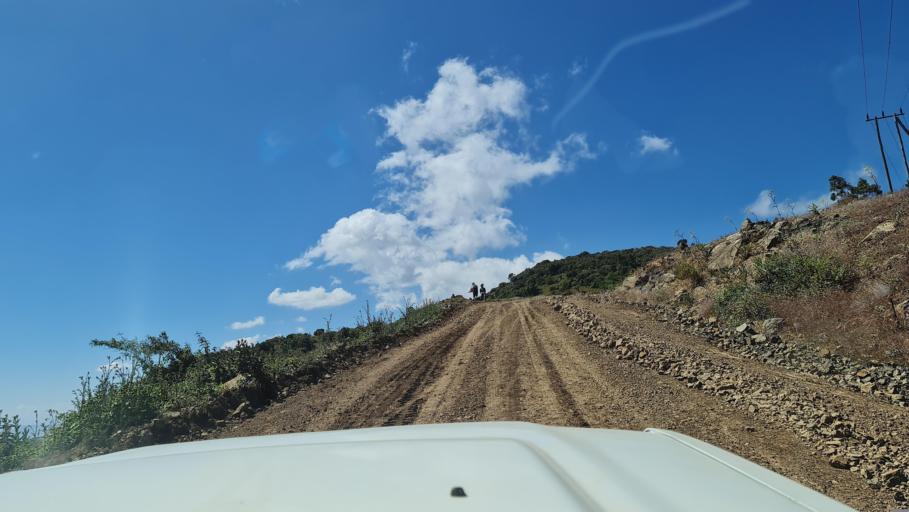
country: ET
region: Amhara
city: Debark'
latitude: 13.2354
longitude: 38.0507
